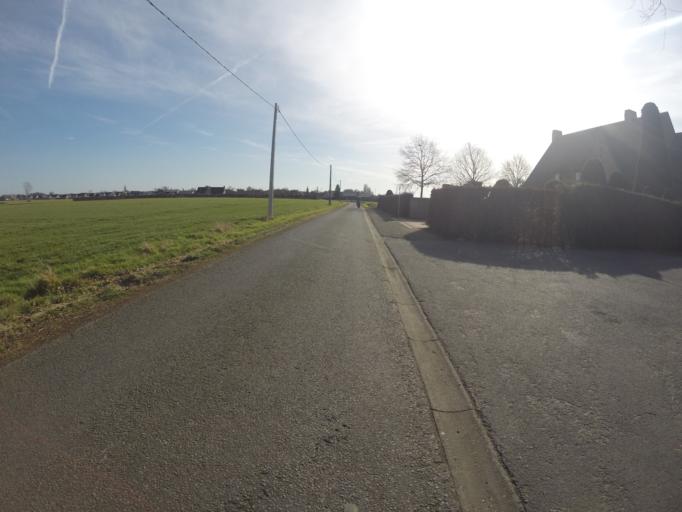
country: BE
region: Flanders
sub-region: Provincie West-Vlaanderen
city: Wingene
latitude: 51.0678
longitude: 3.2706
